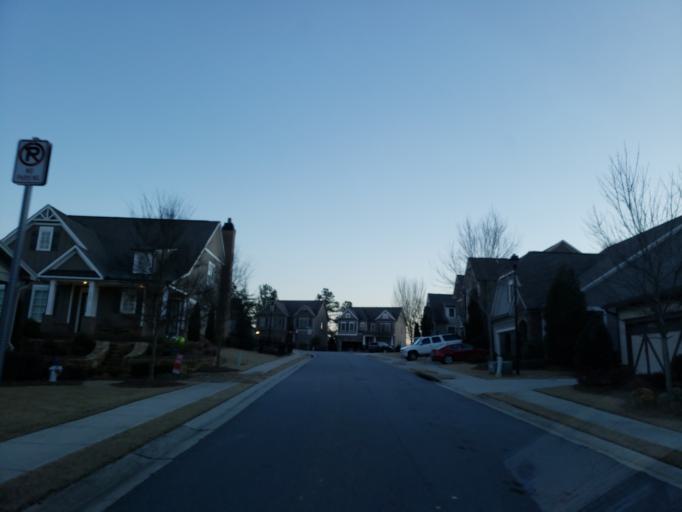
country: US
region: Georgia
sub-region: Cherokee County
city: Woodstock
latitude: 34.0974
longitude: -84.4953
